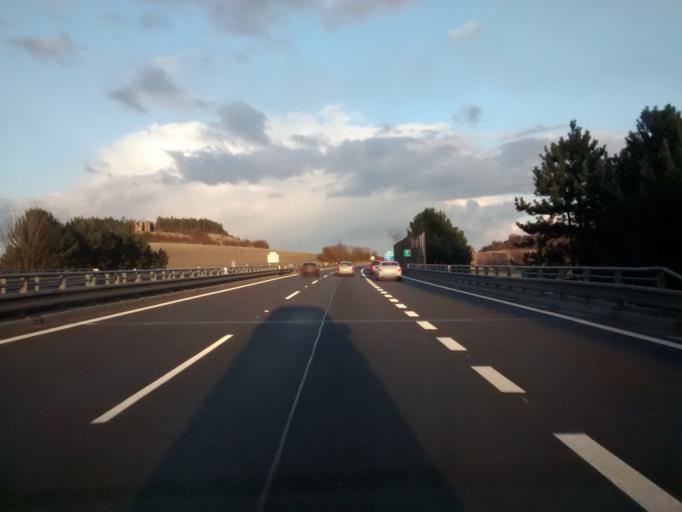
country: CZ
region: Central Bohemia
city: Prerov nad Labem
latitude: 50.1372
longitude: 14.8438
